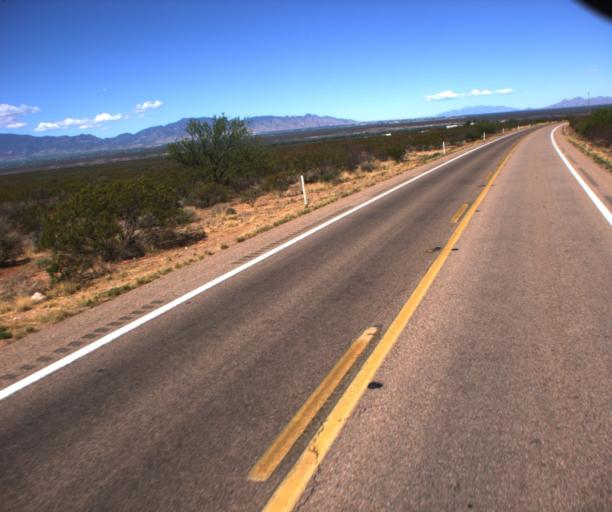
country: US
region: Arizona
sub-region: Cochise County
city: Sierra Vista Southeast
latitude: 31.5450
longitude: -110.0938
